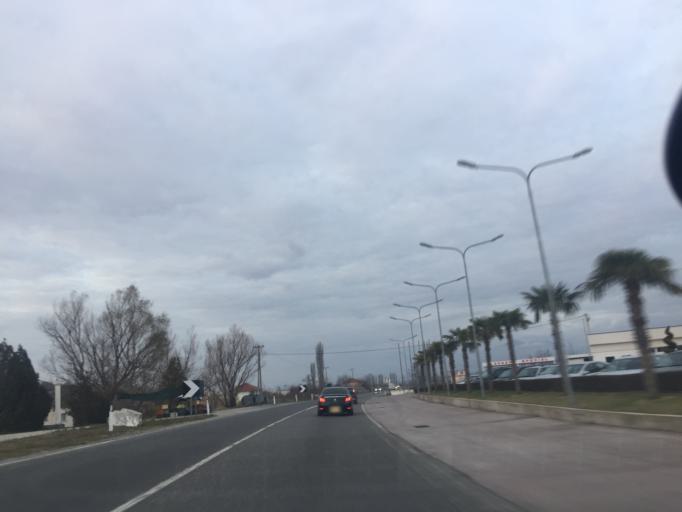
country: AL
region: Shkoder
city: Vukatane
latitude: 41.9696
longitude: 19.5471
